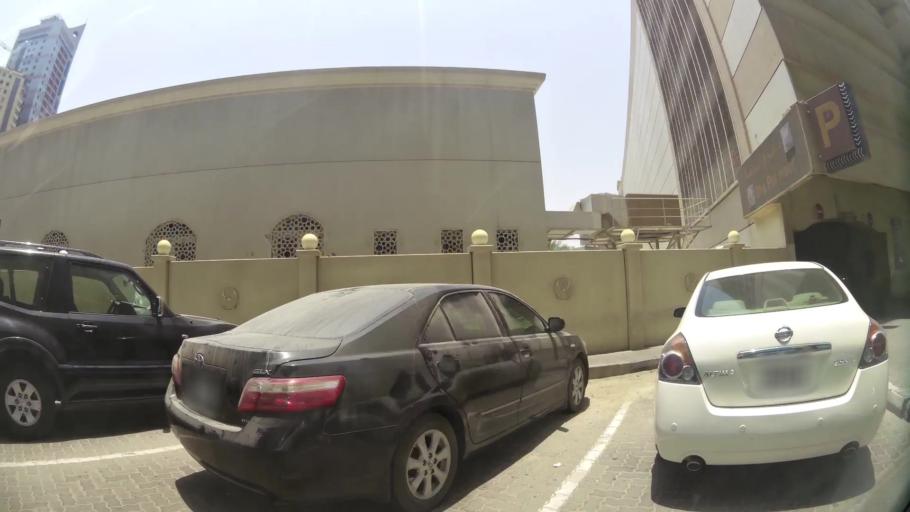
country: AE
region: Ash Shariqah
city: Sharjah
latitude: 25.3233
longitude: 55.3821
